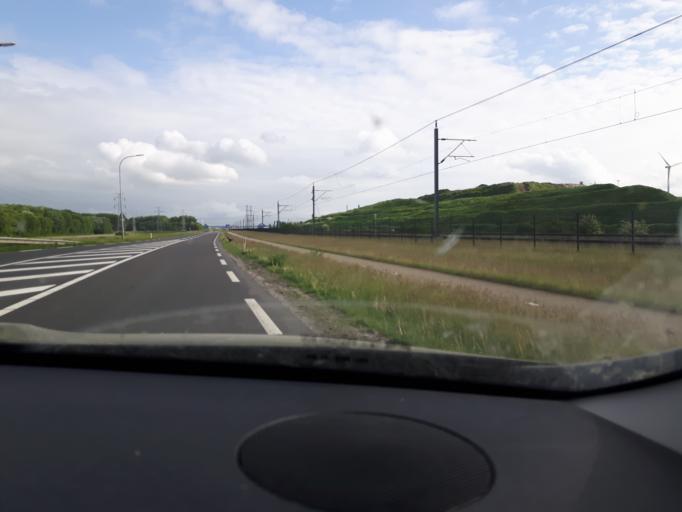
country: NL
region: Zeeland
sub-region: Gemeente Borsele
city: Borssele
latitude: 51.4705
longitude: 3.7249
